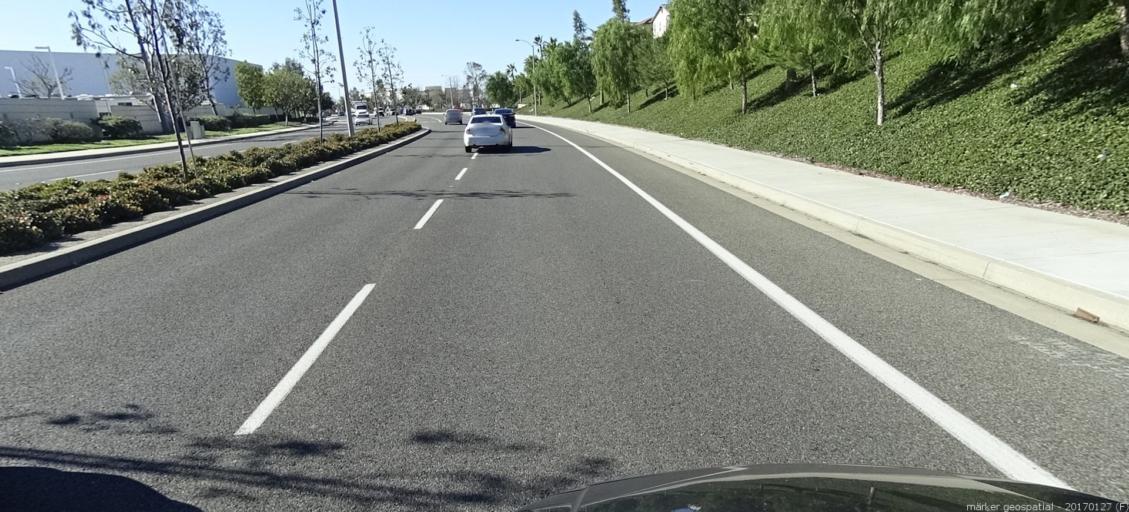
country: US
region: California
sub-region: Orange County
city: Lake Forest
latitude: 33.6679
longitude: -117.6797
